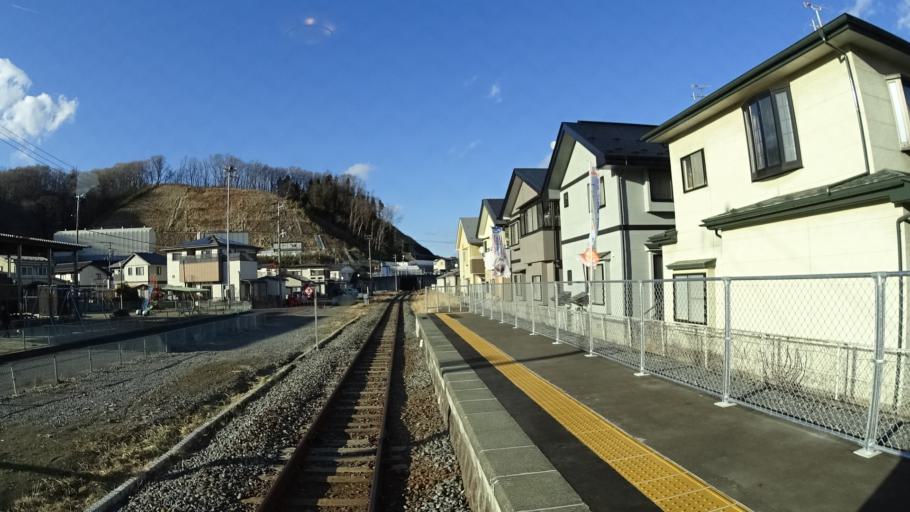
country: JP
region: Iwate
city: Miyako
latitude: 39.6304
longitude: 141.9610
